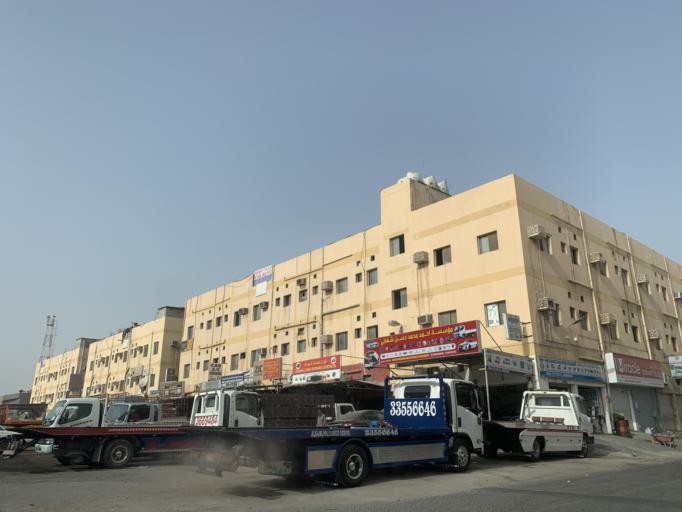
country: BH
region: Northern
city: Madinat `Isa
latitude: 26.1768
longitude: 50.5315
